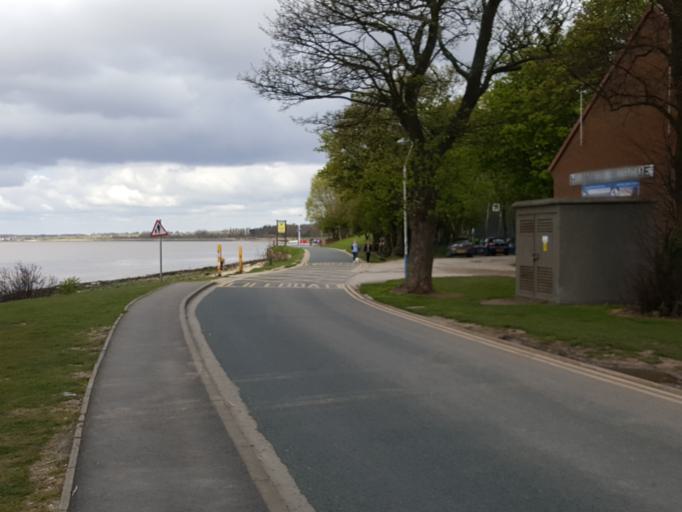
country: GB
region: England
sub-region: East Riding of Yorkshire
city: Hessle
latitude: 53.7144
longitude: -0.4508
